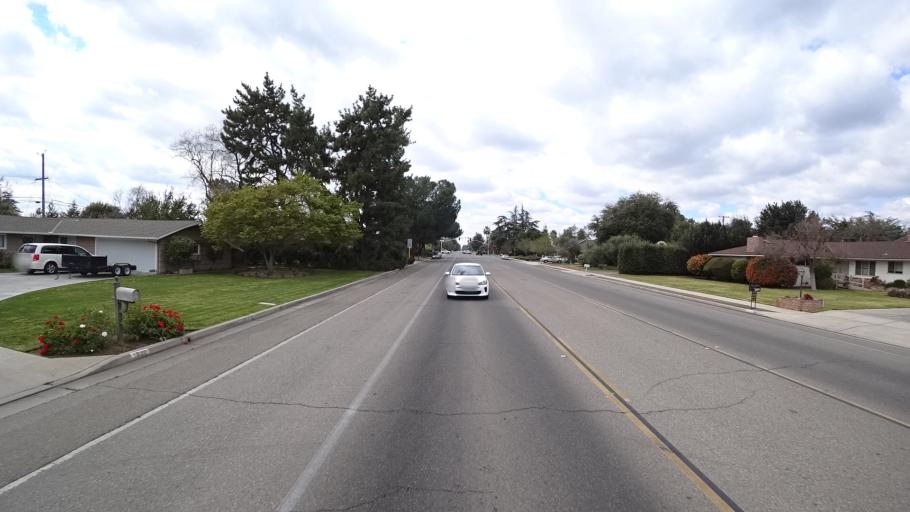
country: US
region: California
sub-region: Fresno County
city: Fresno
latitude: 36.8156
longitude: -119.8157
